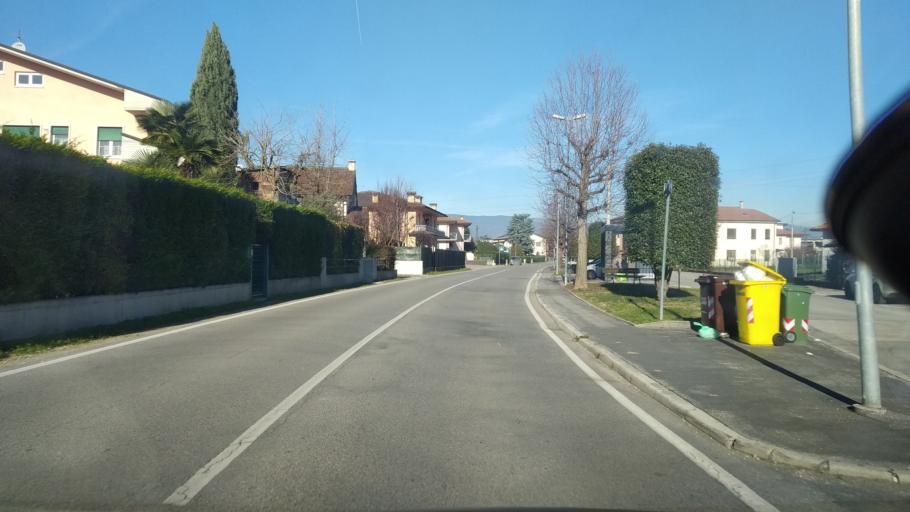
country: IT
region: Veneto
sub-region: Provincia di Vicenza
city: Caldogno-Rettorgole-Cresole
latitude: 45.6173
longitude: 11.5065
